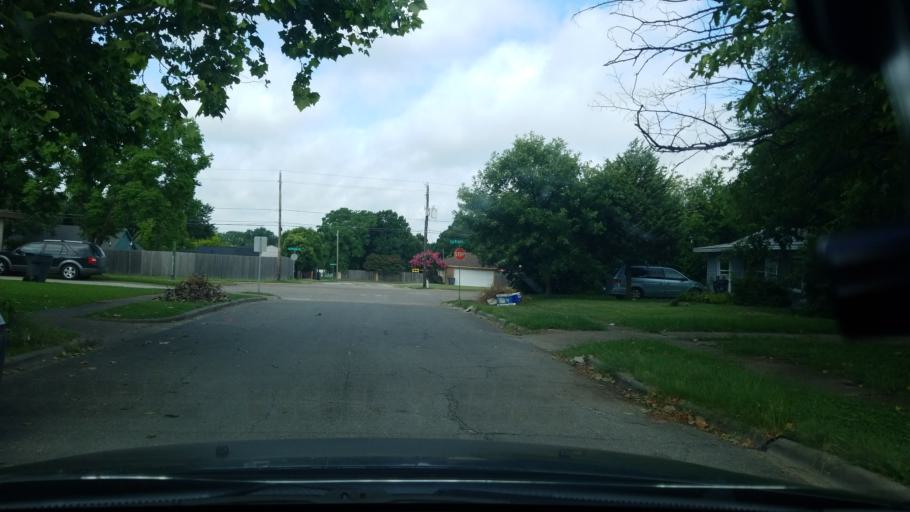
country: US
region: Texas
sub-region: Dallas County
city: Mesquite
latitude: 32.8169
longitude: -96.6647
